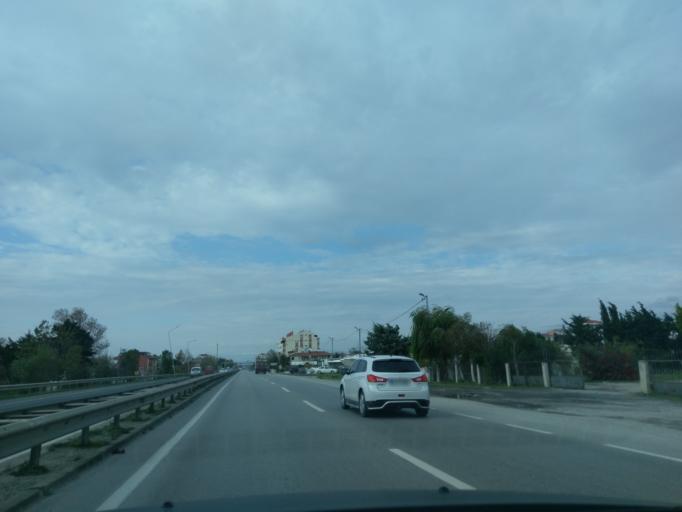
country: TR
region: Istanbul
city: Celaliye
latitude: 41.0426
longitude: 28.4188
